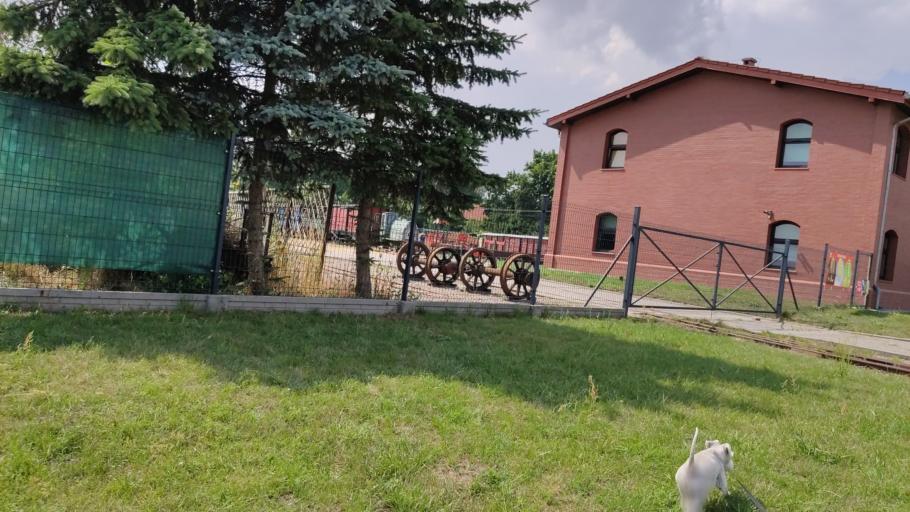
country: PL
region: Kujawsko-Pomorskie
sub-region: Powiat zninski
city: Gasawa
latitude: 52.7984
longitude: 17.7532
